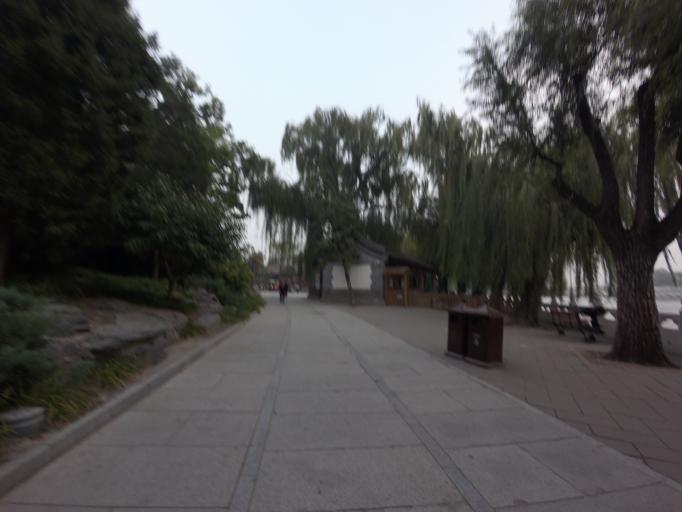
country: CN
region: Beijing
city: Beijing
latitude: 39.9233
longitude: 116.3818
